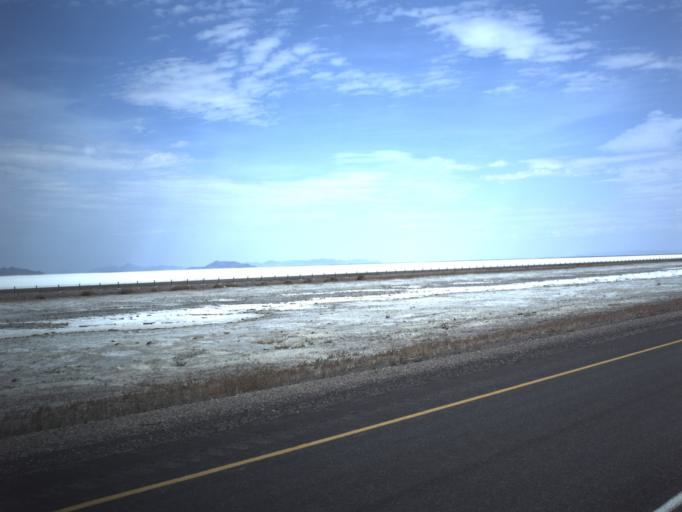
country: US
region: Utah
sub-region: Tooele County
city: Wendover
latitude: 40.7391
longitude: -113.8822
